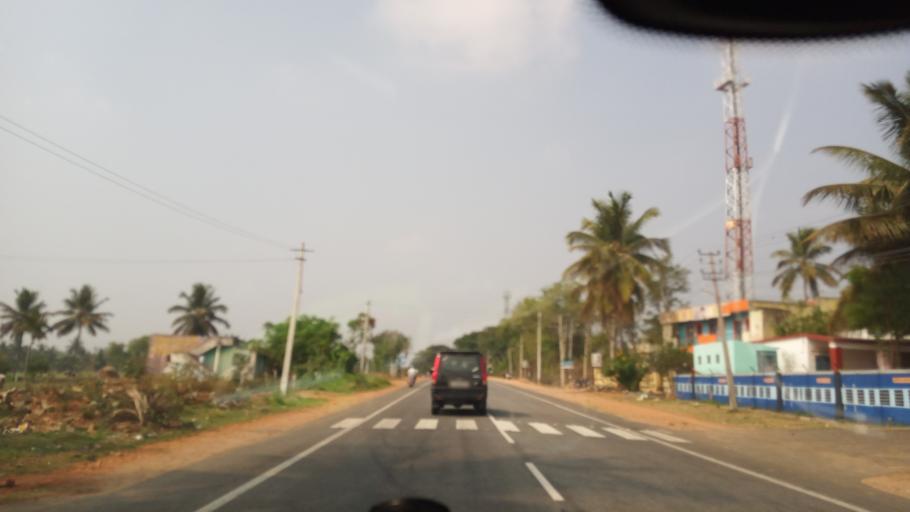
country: IN
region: Karnataka
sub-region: Mandya
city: Nagamangala
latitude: 12.7522
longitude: 76.7294
